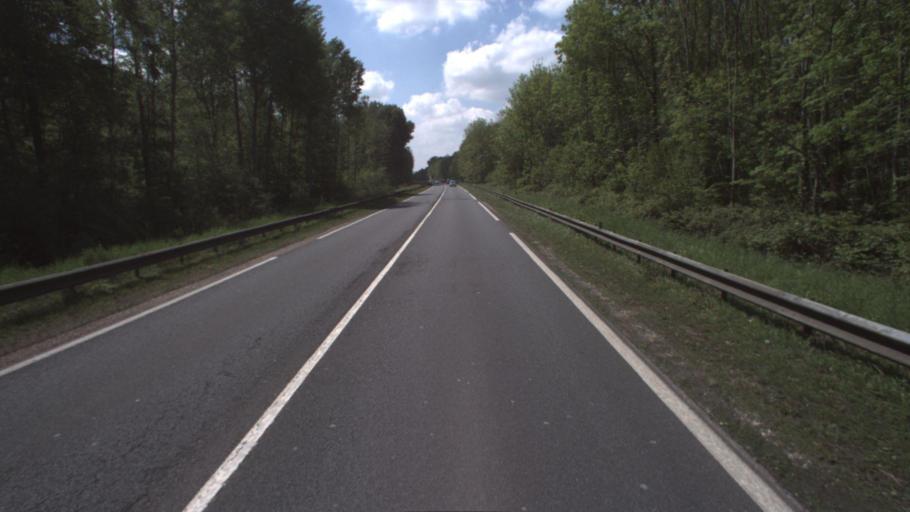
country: FR
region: Ile-de-France
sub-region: Departement de Seine-et-Marne
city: Chaumes-en-Brie
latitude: 48.6890
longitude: 2.8175
